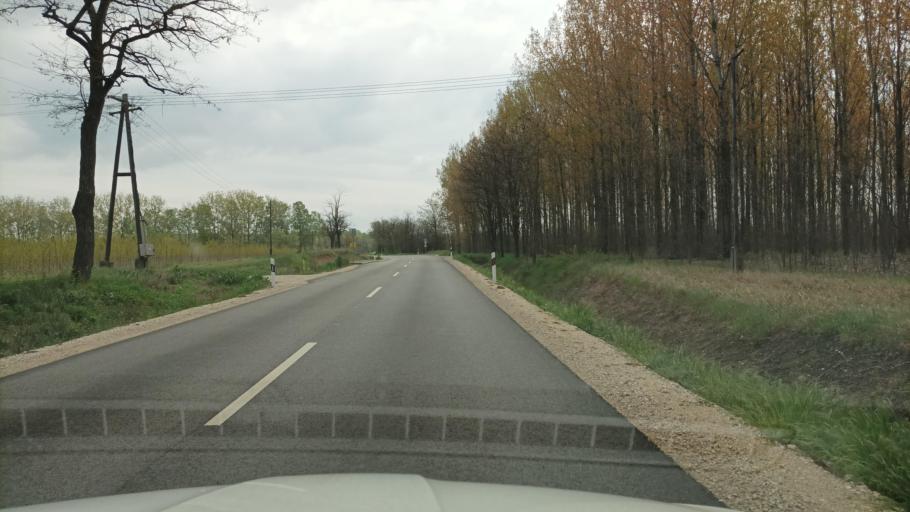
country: HU
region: Pest
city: Kocser
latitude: 47.0157
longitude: 19.8667
